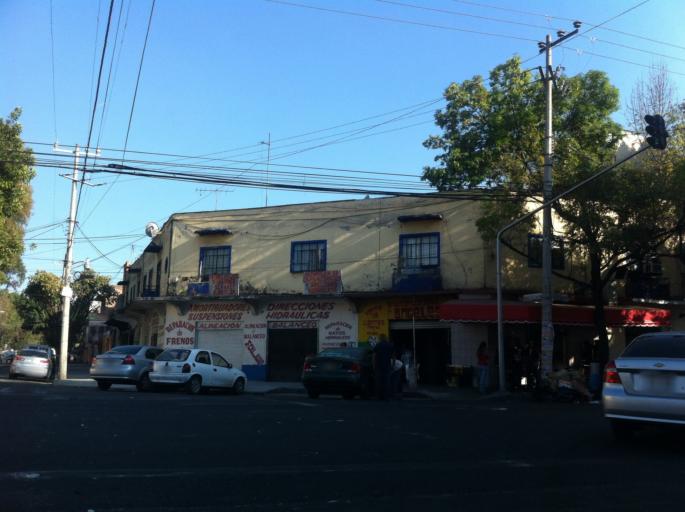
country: MX
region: Mexico City
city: Mexico City
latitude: 19.4157
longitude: -99.1411
